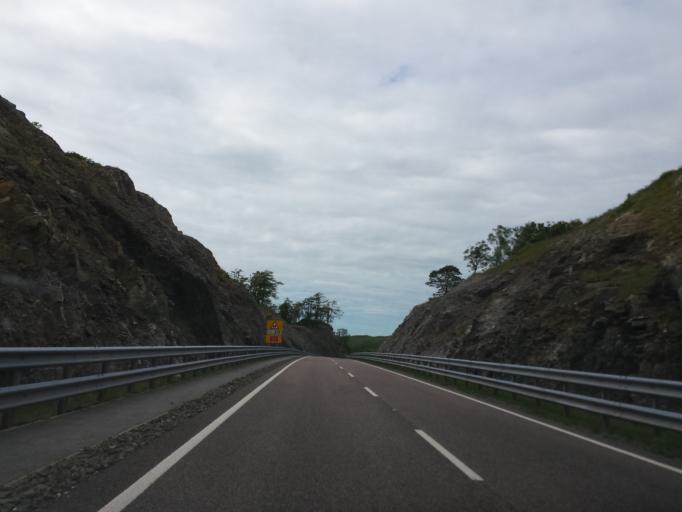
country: GB
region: Scotland
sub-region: Argyll and Bute
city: Isle Of Mull
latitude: 56.9057
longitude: -5.8184
